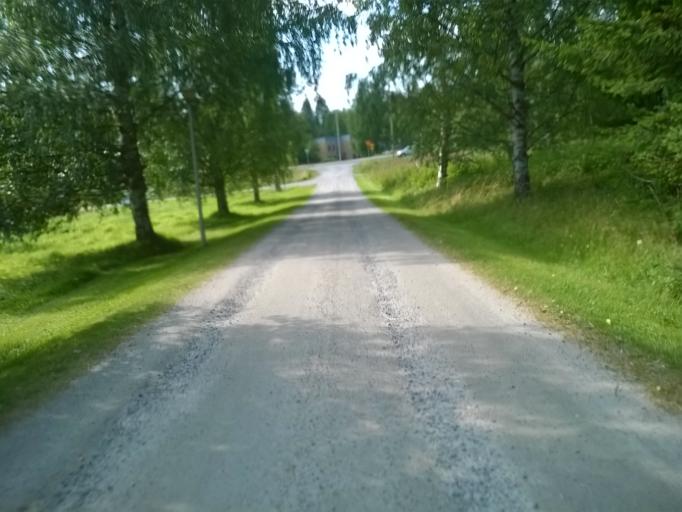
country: FI
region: Kainuu
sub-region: Kehys-Kainuu
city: Kuhmo
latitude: 64.1288
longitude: 29.5036
